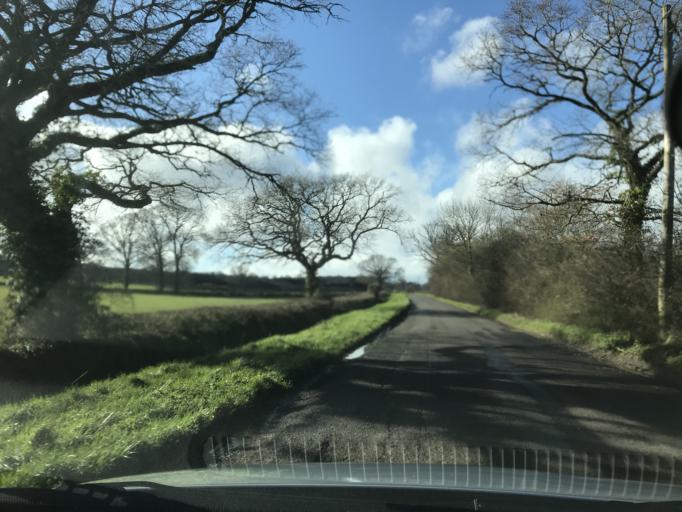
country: GB
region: England
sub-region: Somerset
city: Chard
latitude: 50.9467
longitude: -3.0046
